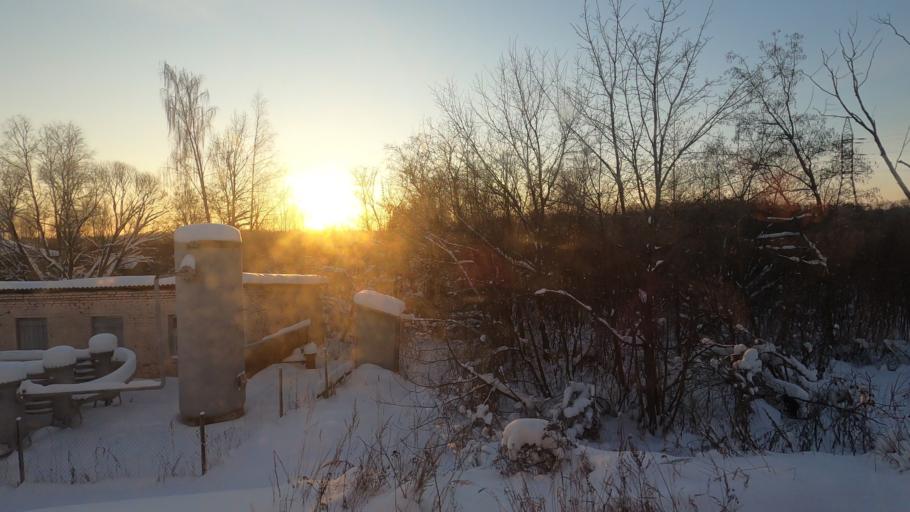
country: RU
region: Moskovskaya
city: Dmitrov
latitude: 56.3845
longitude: 37.5142
